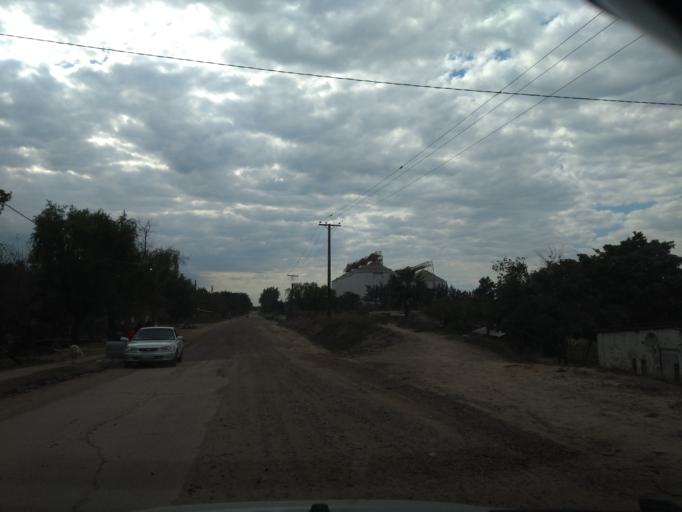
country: AR
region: Chaco
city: Puerto Vilelas
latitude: -27.5356
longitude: -58.9237
